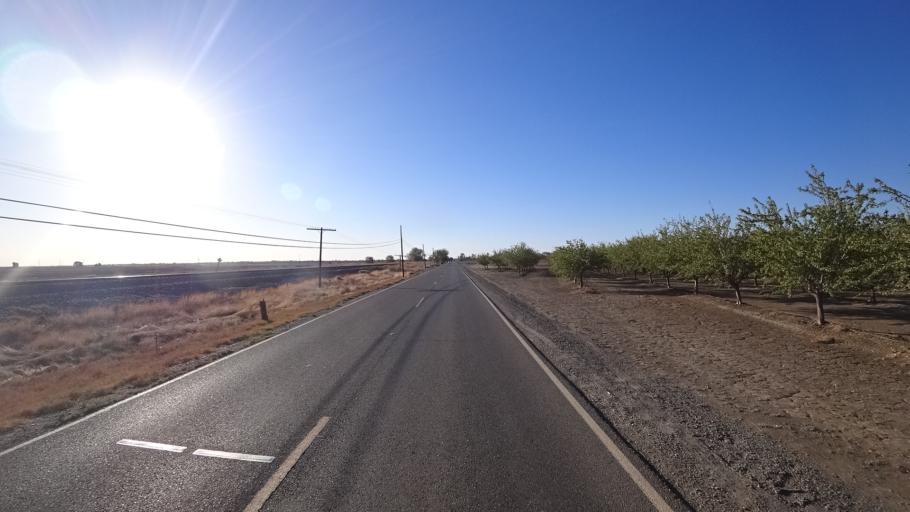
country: US
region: California
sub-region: Yolo County
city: Davis
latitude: 38.5876
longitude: -121.7517
